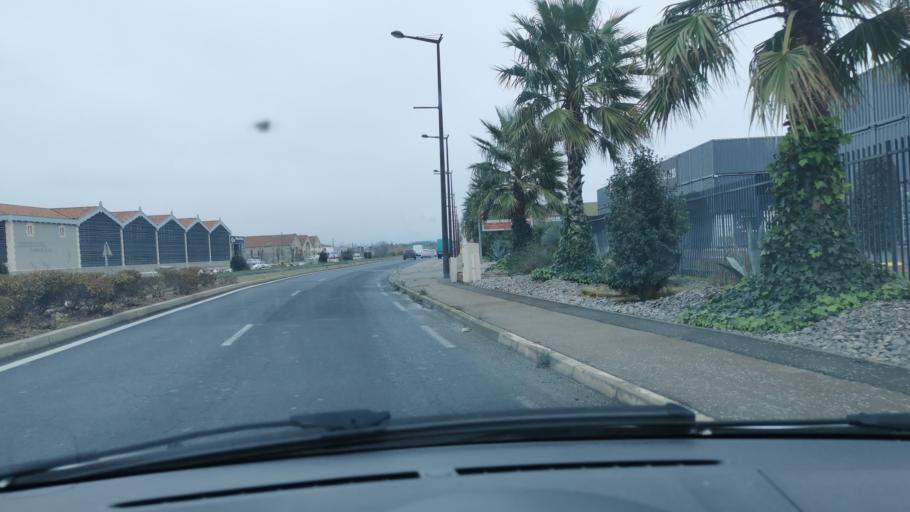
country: FR
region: Languedoc-Roussillon
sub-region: Departement de l'Herault
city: Sete
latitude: 43.4146
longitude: 3.7172
